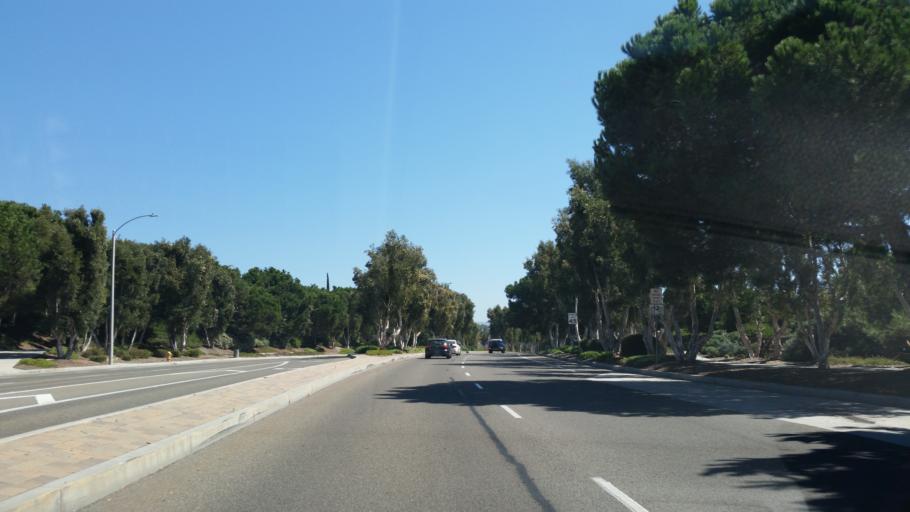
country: US
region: California
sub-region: Orange County
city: San Clemente
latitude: 33.4642
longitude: -117.5973
